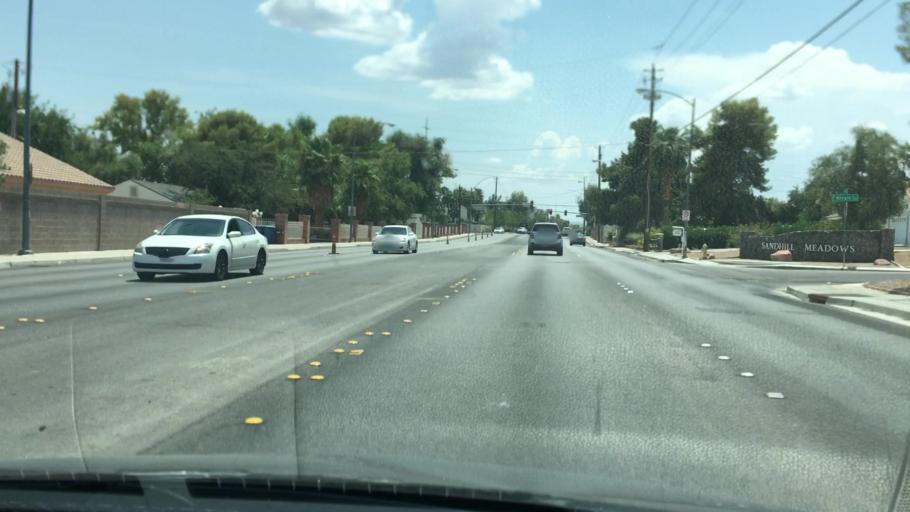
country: US
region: Nevada
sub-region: Clark County
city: Whitney
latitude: 36.0874
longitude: -115.0914
